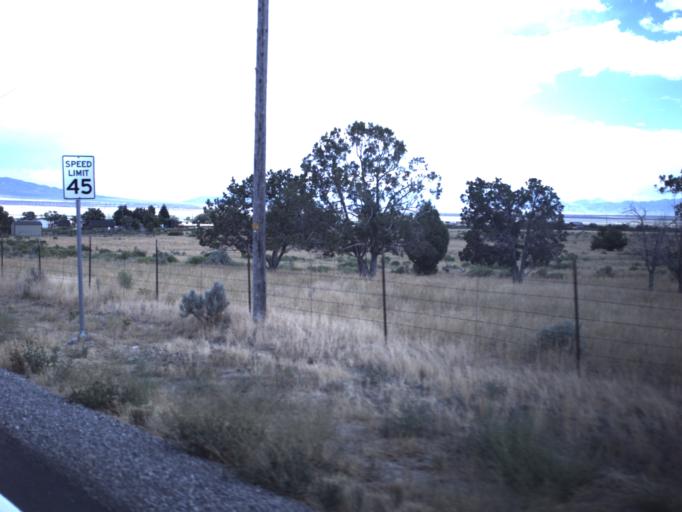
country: US
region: Utah
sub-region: Tooele County
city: Tooele
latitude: 40.3385
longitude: -112.4704
